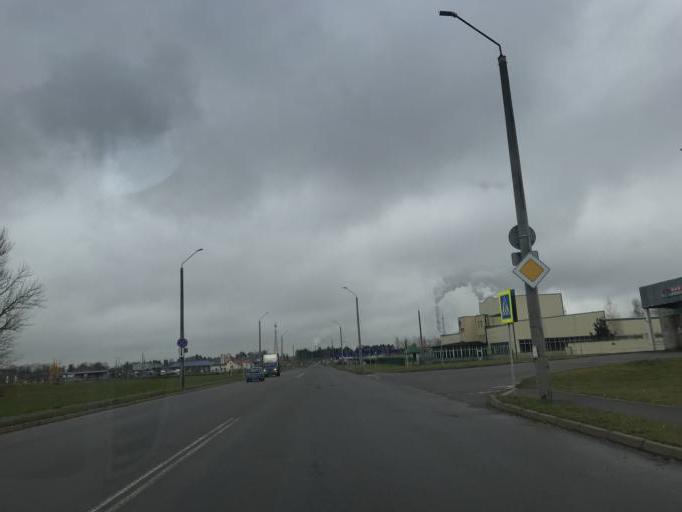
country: BY
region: Mogilev
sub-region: Mahilyowski Rayon
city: Veyno
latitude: 53.8288
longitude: 30.3438
